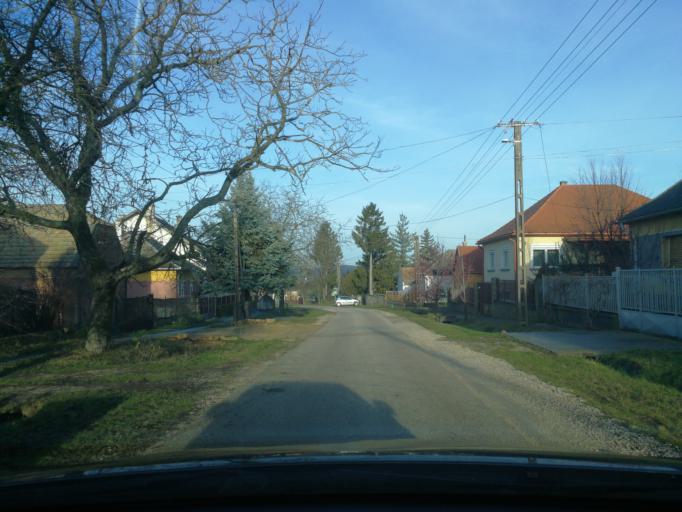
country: HU
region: Veszprem
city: Balatonfured
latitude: 47.0083
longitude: 17.7955
